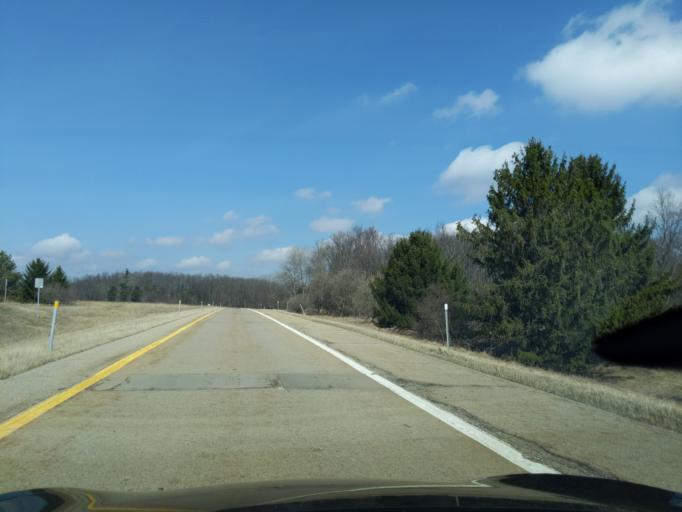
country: US
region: Michigan
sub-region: Calhoun County
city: Marshall
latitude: 42.2989
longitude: -84.9939
